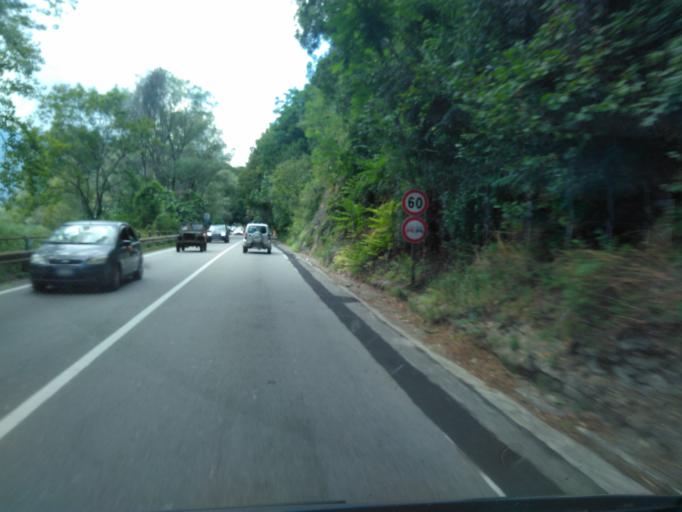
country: IT
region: Piedmont
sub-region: Provincia Verbano-Cusio-Ossola
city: Santino
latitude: 45.9400
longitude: 8.5128
